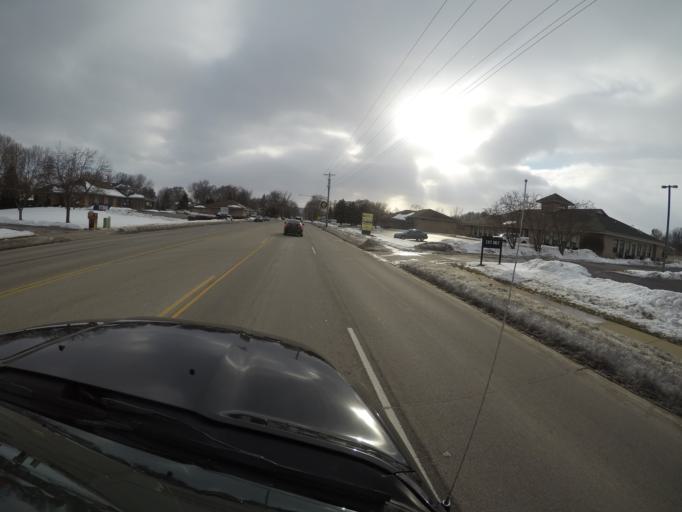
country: US
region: Wisconsin
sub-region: La Crosse County
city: Onalaska
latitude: 43.8821
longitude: -91.2086
